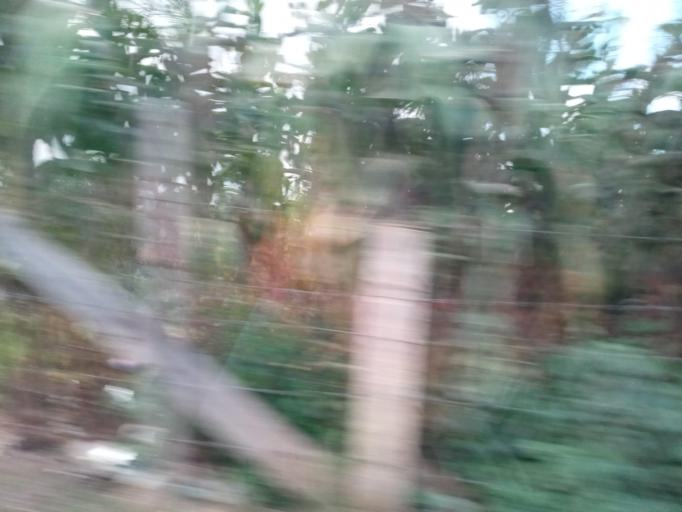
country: GT
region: Quetzaltenango
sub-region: Municipio de La Esperanza
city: La Esperanza
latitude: 14.8478
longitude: -91.5520
